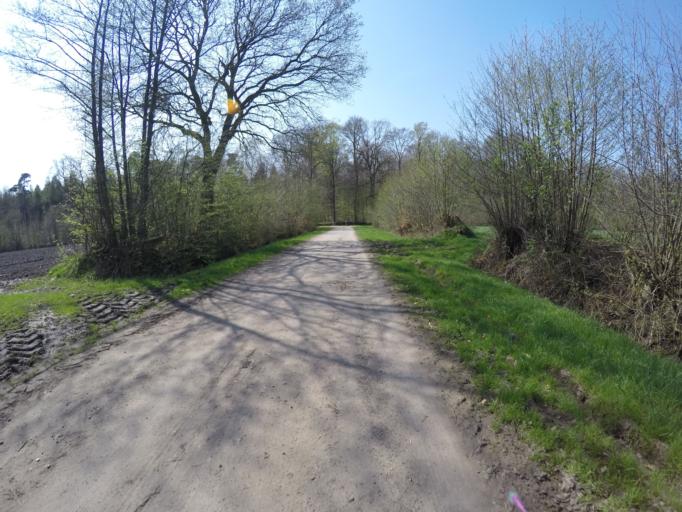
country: DE
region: Schleswig-Holstein
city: Hemdingen
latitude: 53.7499
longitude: 9.8338
